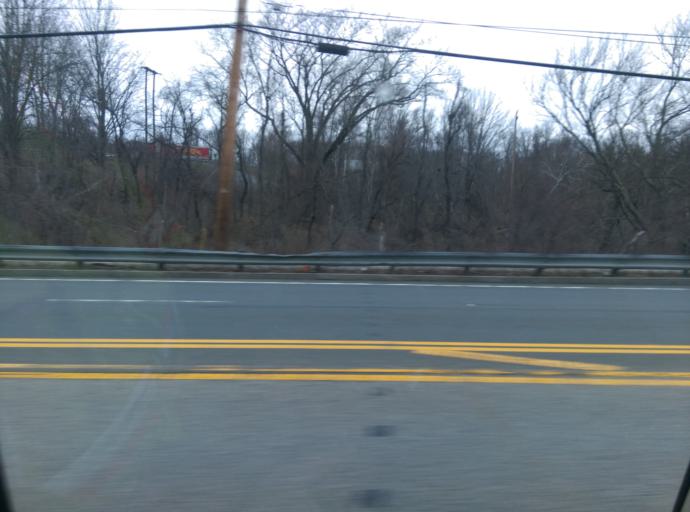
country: US
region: Massachusetts
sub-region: Essex County
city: Amesbury
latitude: 42.8465
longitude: -70.9165
